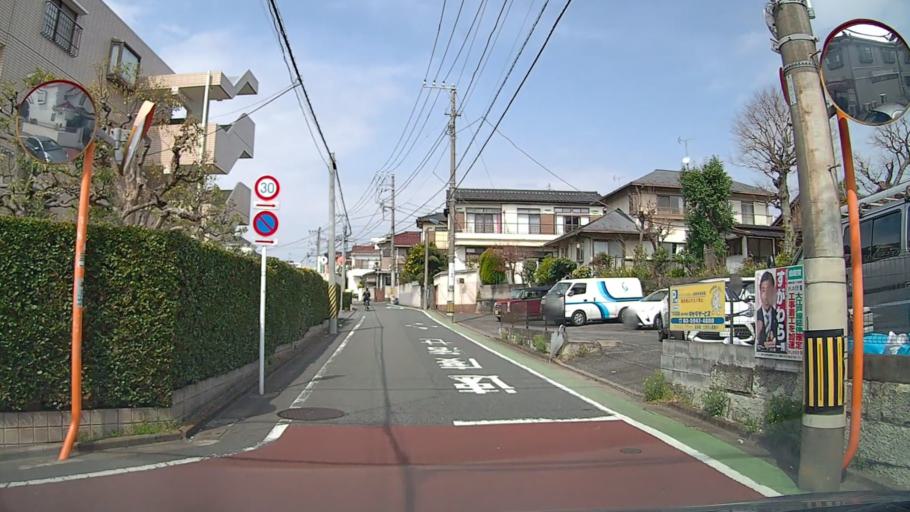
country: JP
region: Saitama
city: Wako
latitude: 35.7602
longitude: 139.5931
